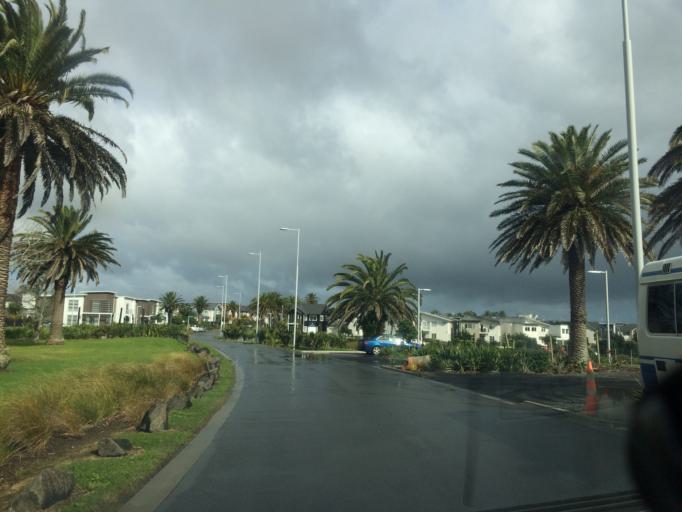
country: NZ
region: Auckland
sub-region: Auckland
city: Rosebank
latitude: -36.7906
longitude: 174.6601
